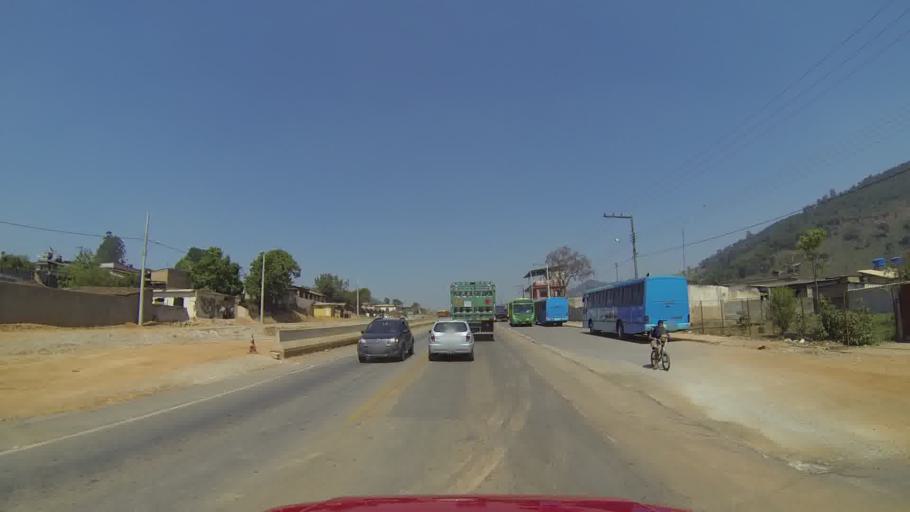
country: BR
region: Minas Gerais
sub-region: Belo Horizonte
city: Belo Horizonte
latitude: -19.9237
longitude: -43.9409
